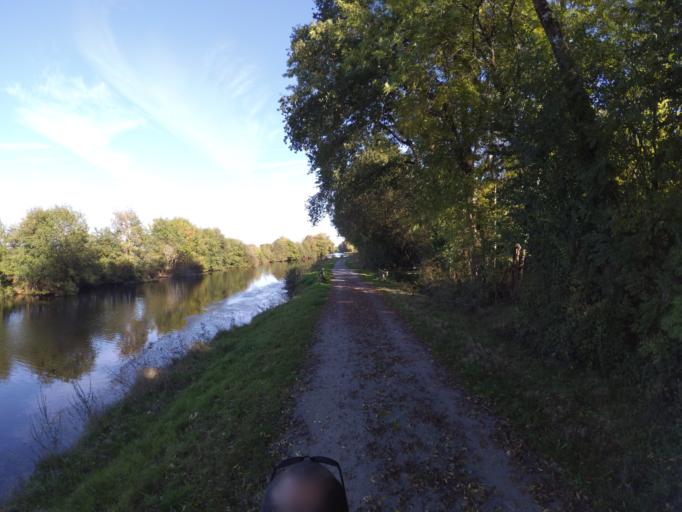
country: FR
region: Brittany
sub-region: Departement du Morbihan
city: Peillac
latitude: 47.7241
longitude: -2.1996
